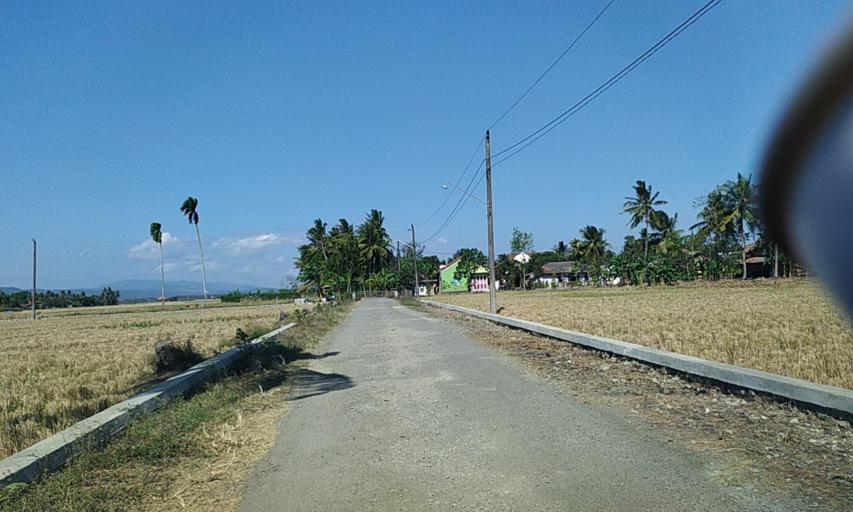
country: ID
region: Central Java
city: Penisihan
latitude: -7.5940
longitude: 109.1718
